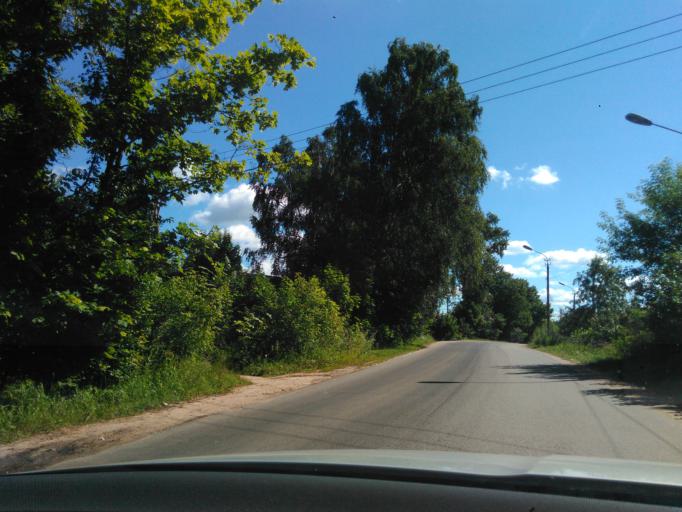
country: RU
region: Moskovskaya
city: Klin
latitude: 56.2365
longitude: 36.8305
